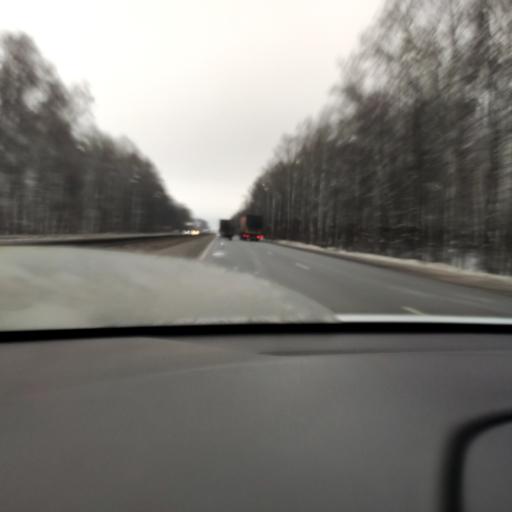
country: RU
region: Tatarstan
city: Osinovo
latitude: 55.8414
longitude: 48.8516
